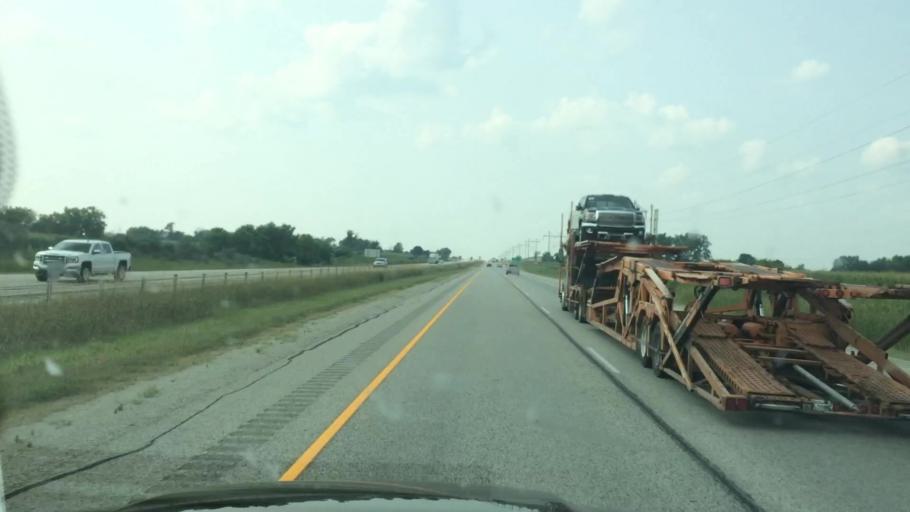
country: US
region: Wisconsin
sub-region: Fond du Lac County
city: North Fond du Lac
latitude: 43.8417
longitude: -88.5568
